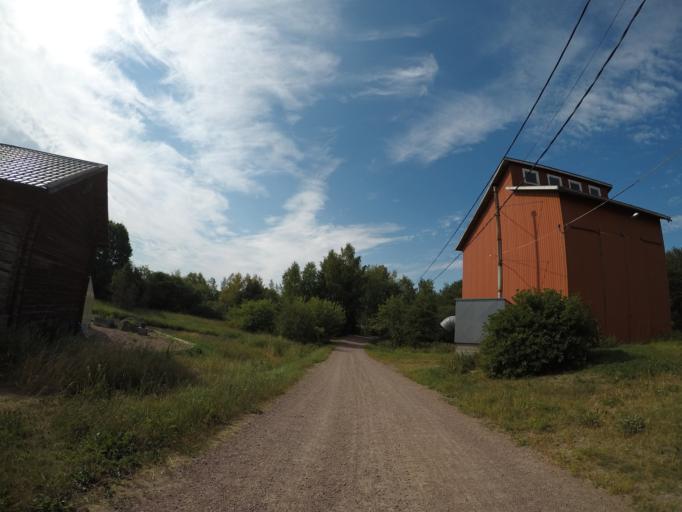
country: AX
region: Alands landsbygd
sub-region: Finstroem
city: Finstroem
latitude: 60.2274
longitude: 19.8503
